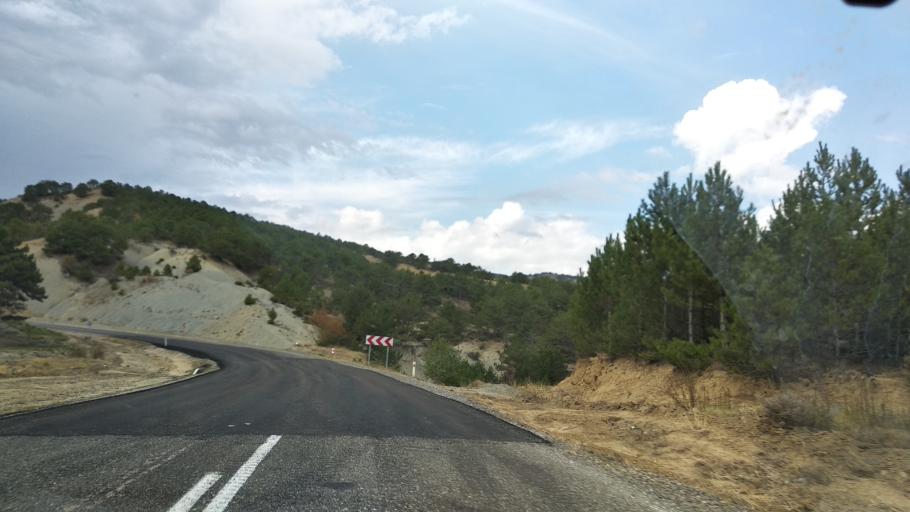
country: TR
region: Bolu
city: Seben
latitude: 40.3594
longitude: 31.4825
